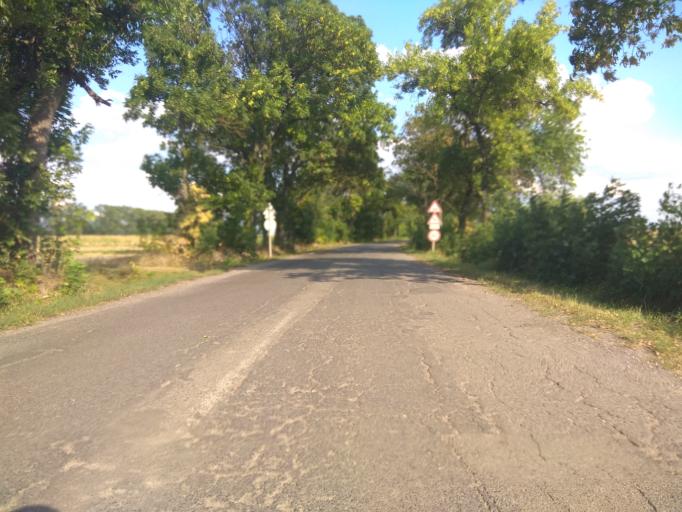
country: HU
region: Borsod-Abauj-Zemplen
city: Mezocsat
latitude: 47.8188
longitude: 20.8679
